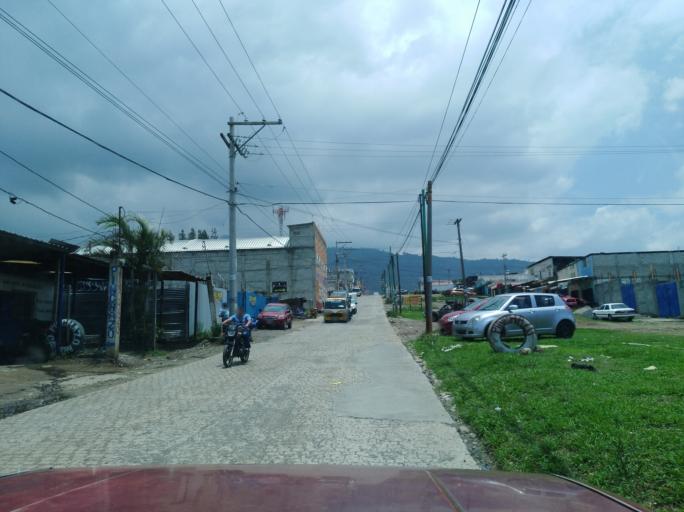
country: GT
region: Guatemala
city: Villa Nueva
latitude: 14.5282
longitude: -90.6213
